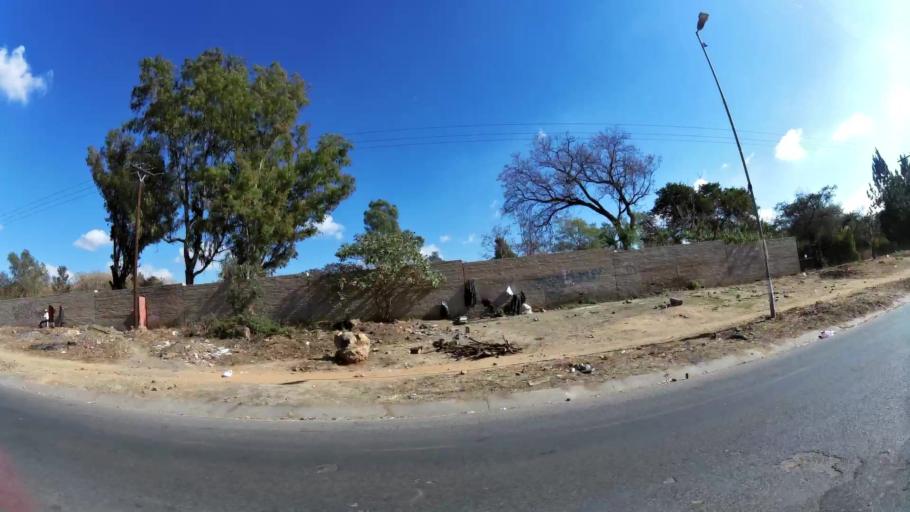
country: ZA
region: Gauteng
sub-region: West Rand District Municipality
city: Muldersdriseloop
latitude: -26.0569
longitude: 27.9035
